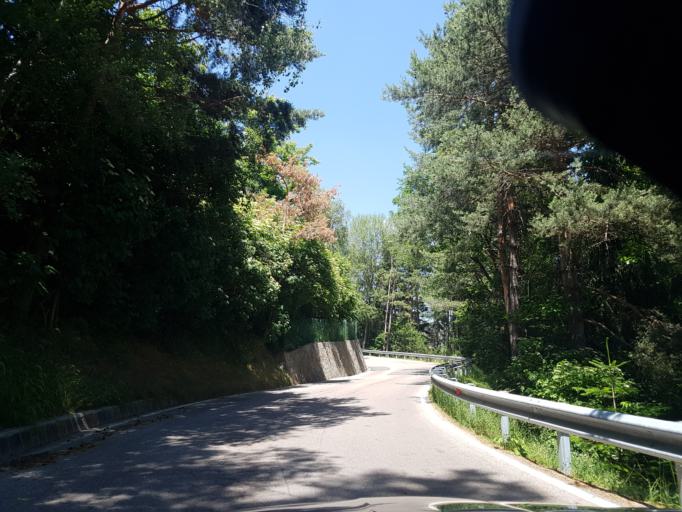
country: IT
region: Trentino-Alto Adige
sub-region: Bolzano
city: Villandro - Villanders
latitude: 46.6280
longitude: 11.5251
